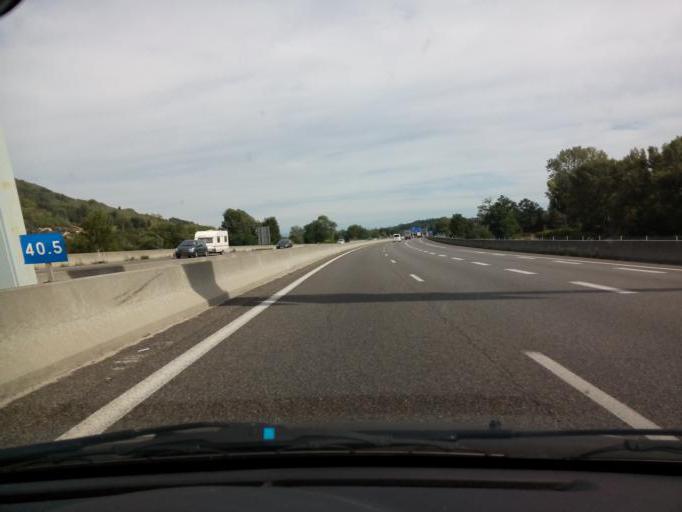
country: FR
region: Rhone-Alpes
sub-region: Departement de l'Isere
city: Ruy
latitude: 45.5710
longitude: 5.3324
